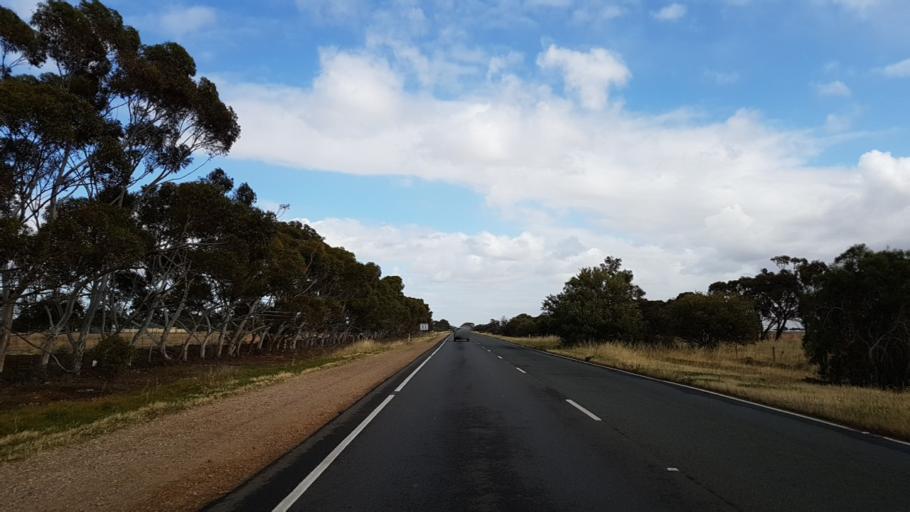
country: AU
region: South Australia
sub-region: Mallala
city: Two Wells
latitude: -34.6318
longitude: 138.5271
